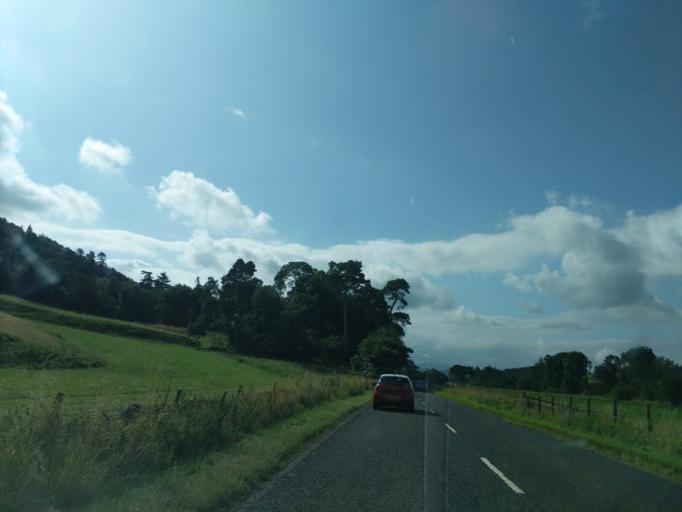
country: GB
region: Scotland
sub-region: The Scottish Borders
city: Peebles
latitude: 55.7328
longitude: -3.2061
